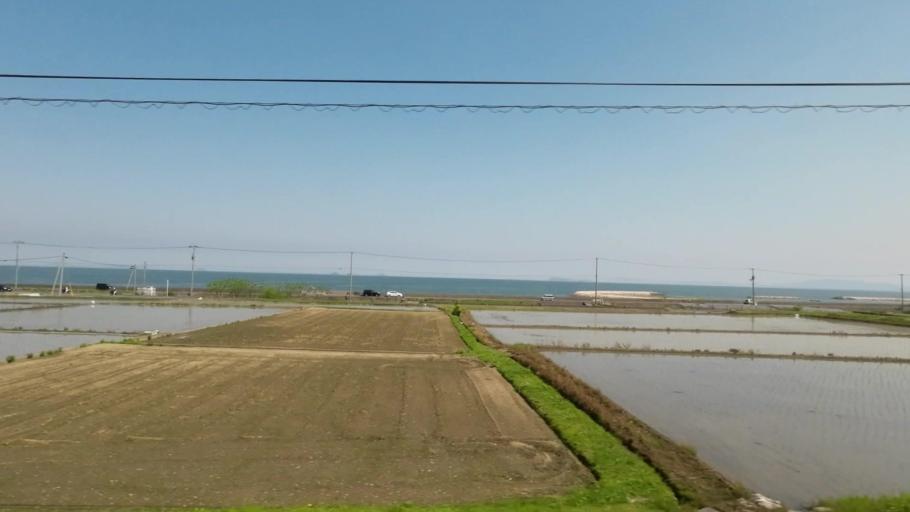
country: JP
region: Ehime
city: Kawanoecho
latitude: 33.9677
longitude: 133.4938
